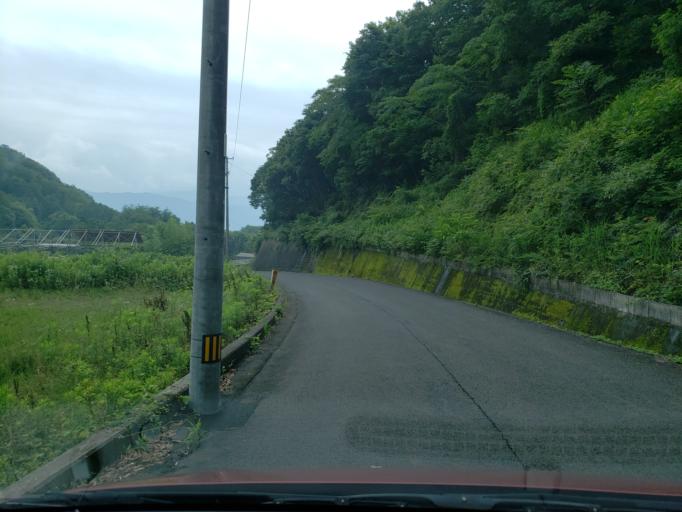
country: JP
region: Tokushima
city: Kamojimacho-jogejima
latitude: 34.1087
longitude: 134.2983
